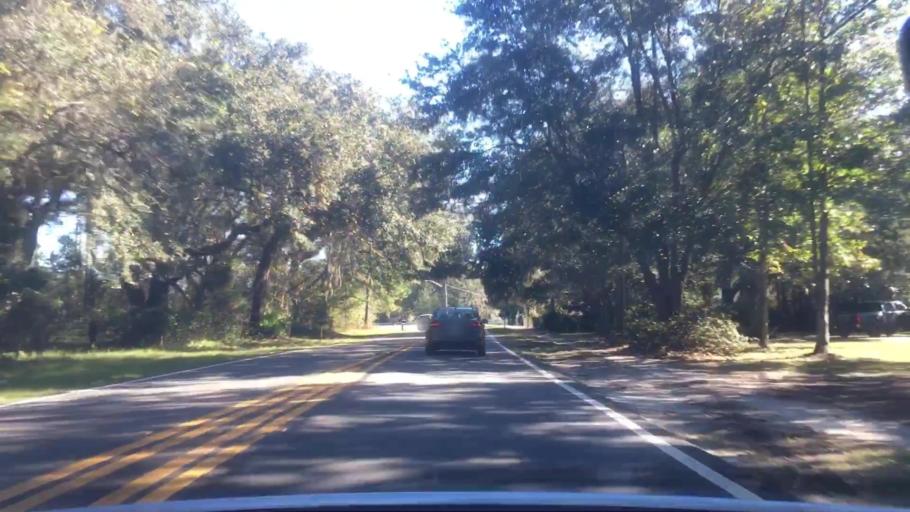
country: US
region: Florida
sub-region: Nassau County
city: Yulee
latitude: 30.4842
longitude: -81.5947
